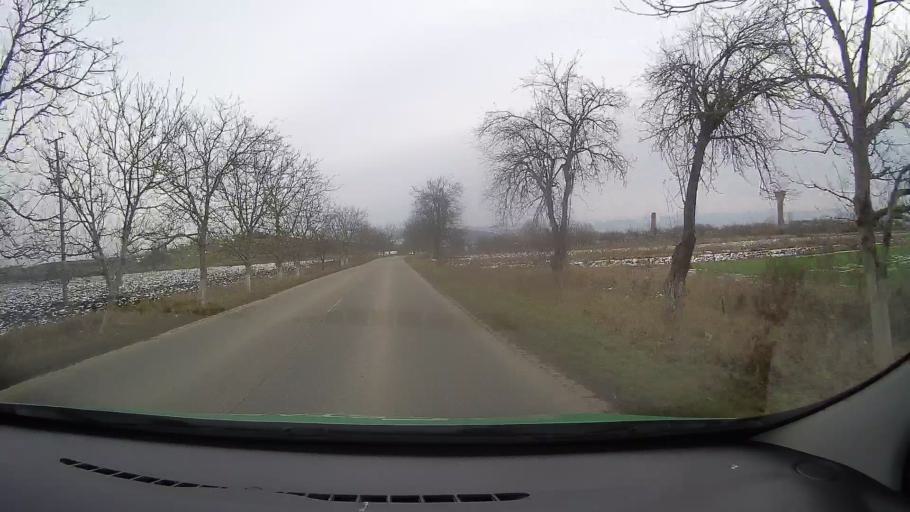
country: RO
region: Hunedoara
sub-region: Comuna Romos
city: Romos
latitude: 45.8812
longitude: 23.2560
